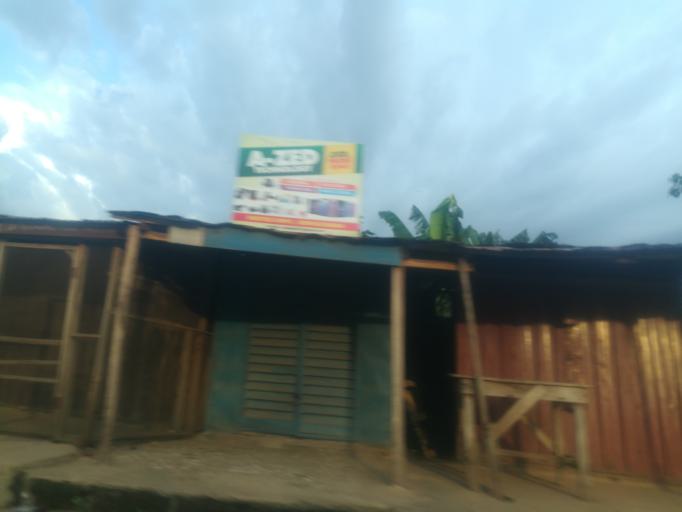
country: NG
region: Oyo
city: Ibadan
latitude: 7.3841
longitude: 3.8363
